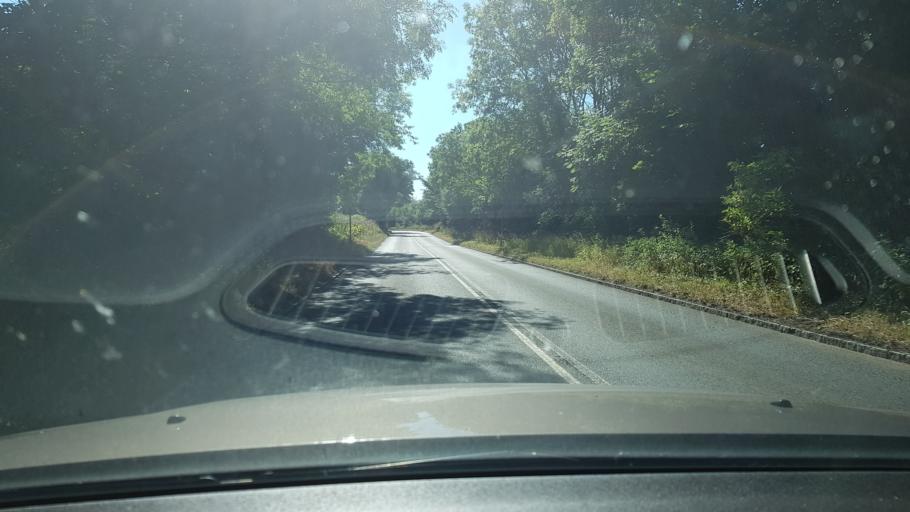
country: GB
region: England
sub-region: Wiltshire
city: Chilton Foliat
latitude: 51.4666
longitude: -1.5038
